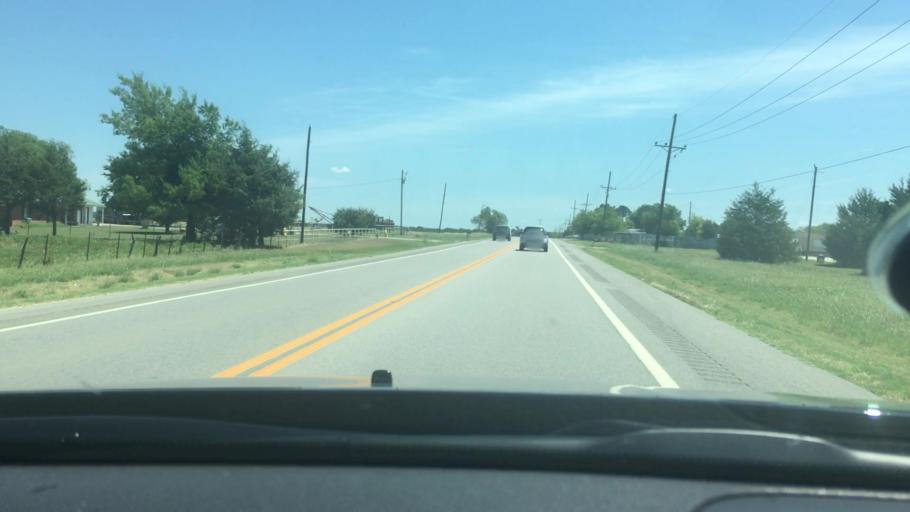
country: US
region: Oklahoma
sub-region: Bryan County
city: Durant
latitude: 34.0093
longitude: -96.1743
